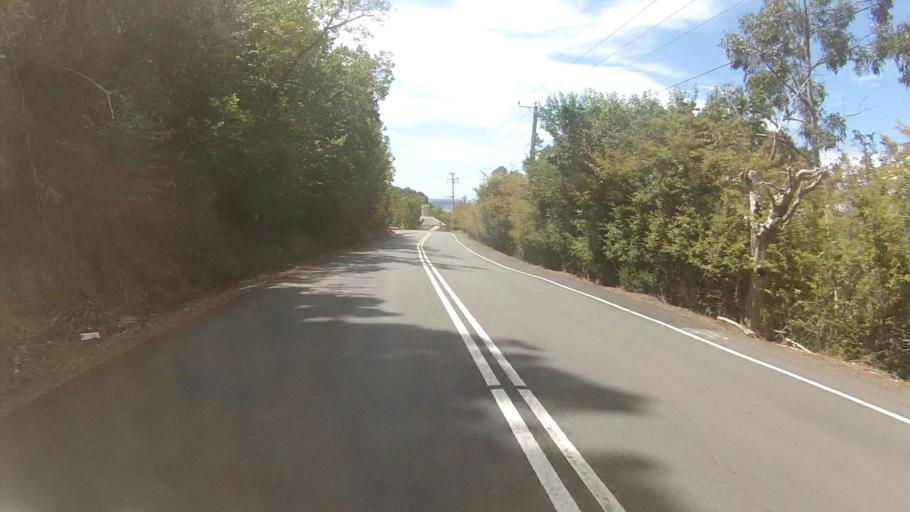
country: AU
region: Tasmania
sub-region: Kingborough
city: Taroona
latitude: -42.9589
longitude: 147.3356
